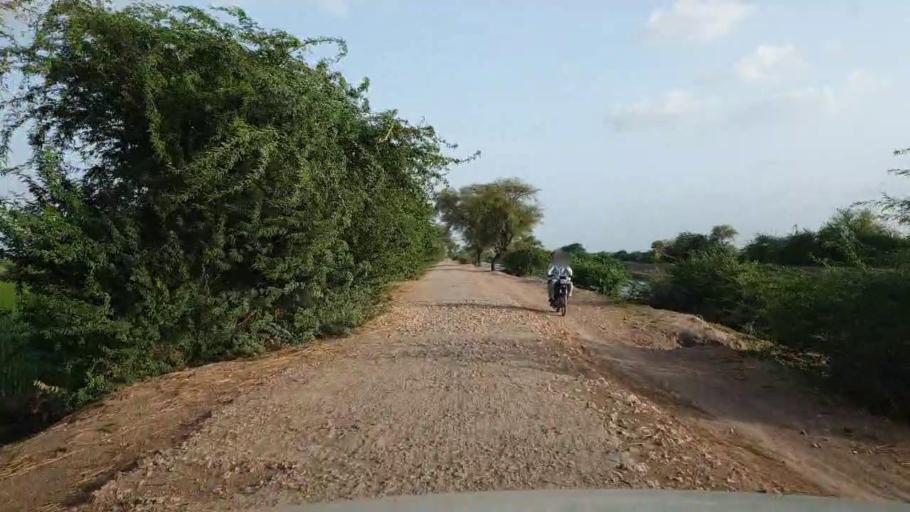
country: PK
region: Sindh
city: Kario
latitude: 24.7981
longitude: 68.6476
